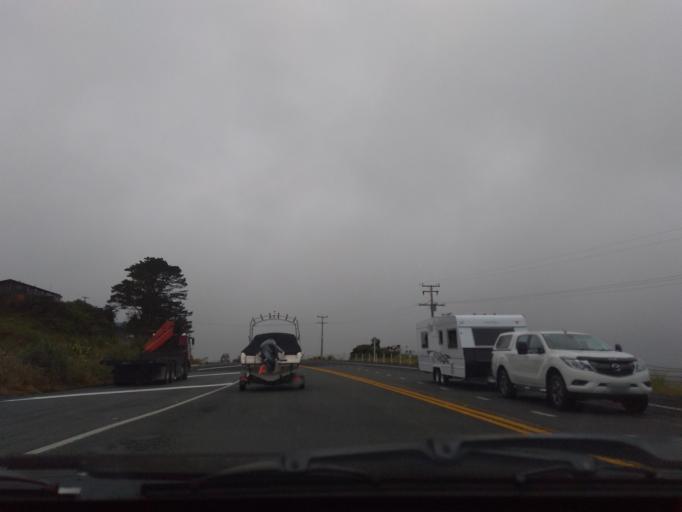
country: NZ
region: Northland
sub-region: Whangarei
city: Ruakaka
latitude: -36.0679
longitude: 174.4220
